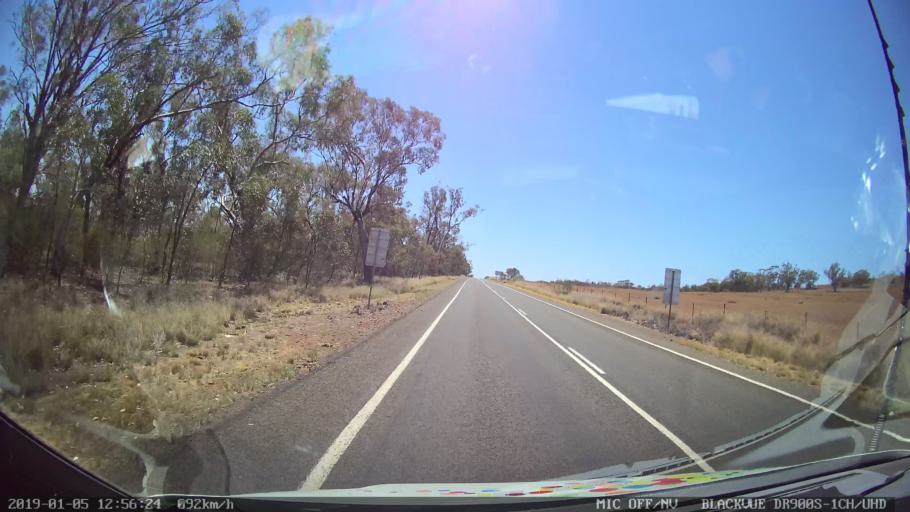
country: AU
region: New South Wales
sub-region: Warrumbungle Shire
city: Coonabarabran
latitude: -31.1146
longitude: 149.7193
